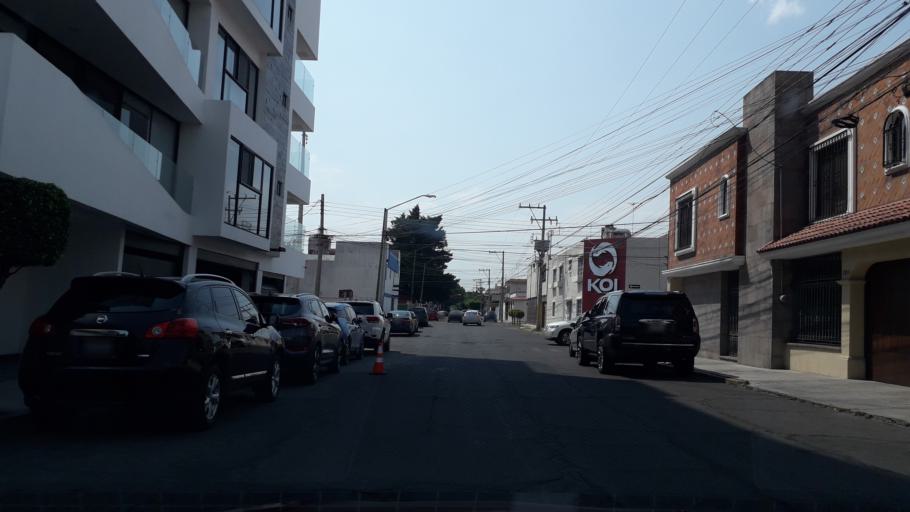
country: MX
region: Puebla
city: Puebla
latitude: 19.0418
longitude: -98.2275
